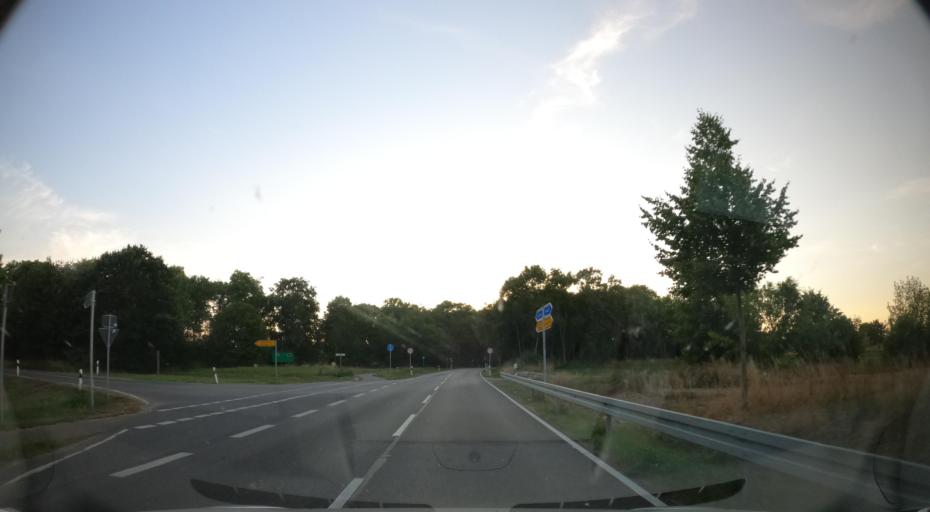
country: DE
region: Mecklenburg-Vorpommern
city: Strasburg
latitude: 53.5019
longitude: 13.7585
